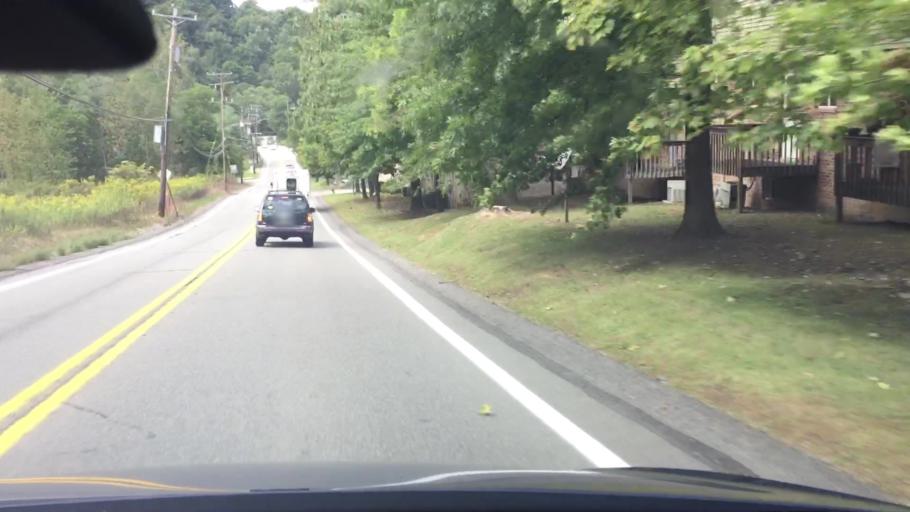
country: US
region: Pennsylvania
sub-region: Allegheny County
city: Cheswick
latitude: 40.5130
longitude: -79.8022
